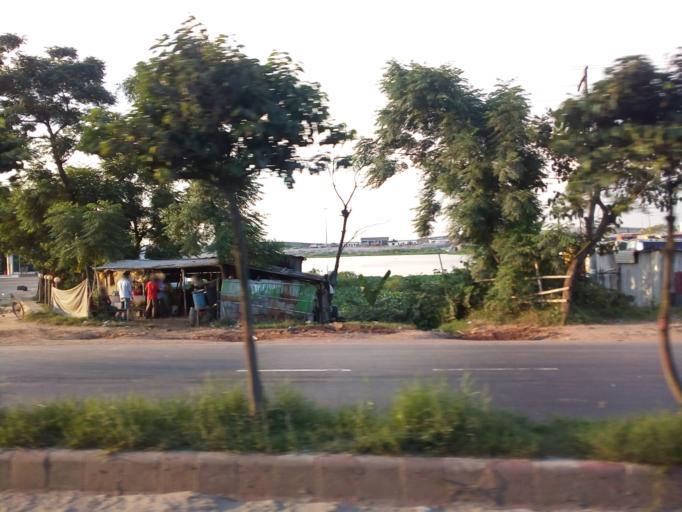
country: BD
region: Dhaka
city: Azimpur
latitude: 23.7933
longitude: 90.2987
